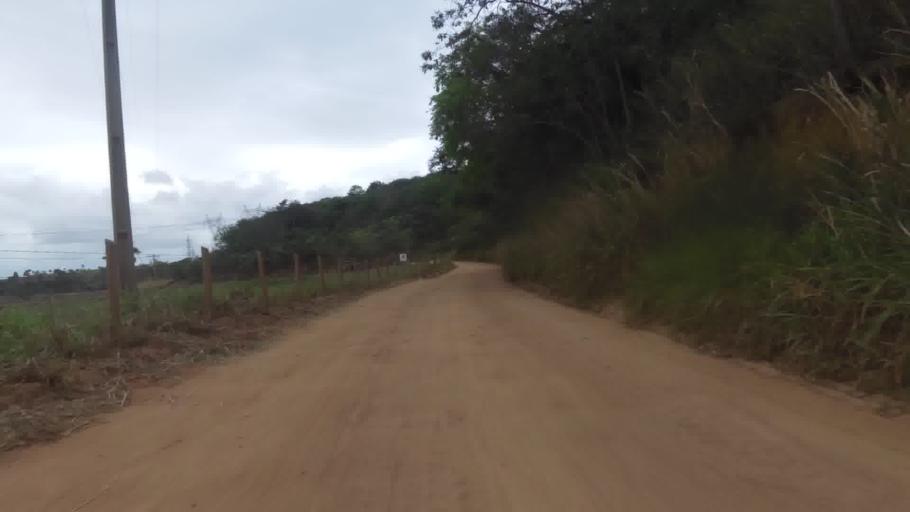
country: BR
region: Espirito Santo
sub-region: Viana
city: Viana
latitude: -20.5206
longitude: -40.4739
